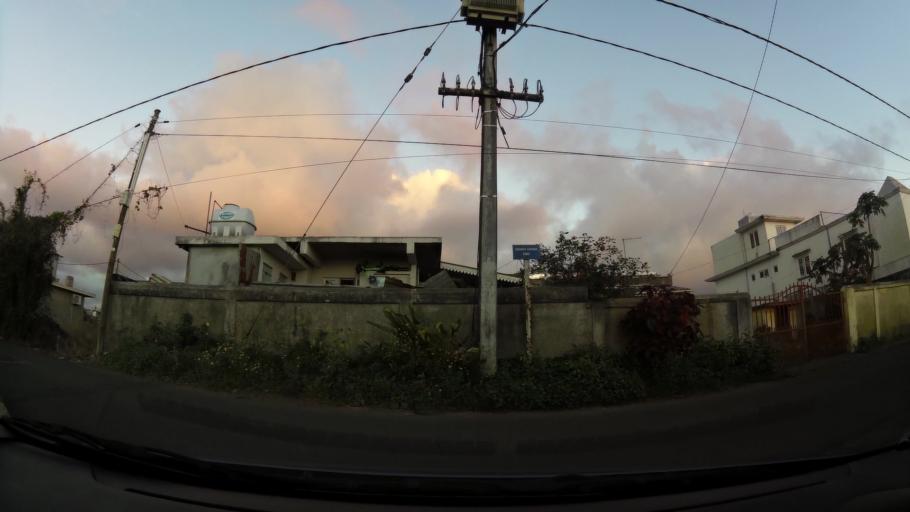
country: MU
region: Plaines Wilhems
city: Curepipe
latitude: -20.3002
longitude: 57.5260
